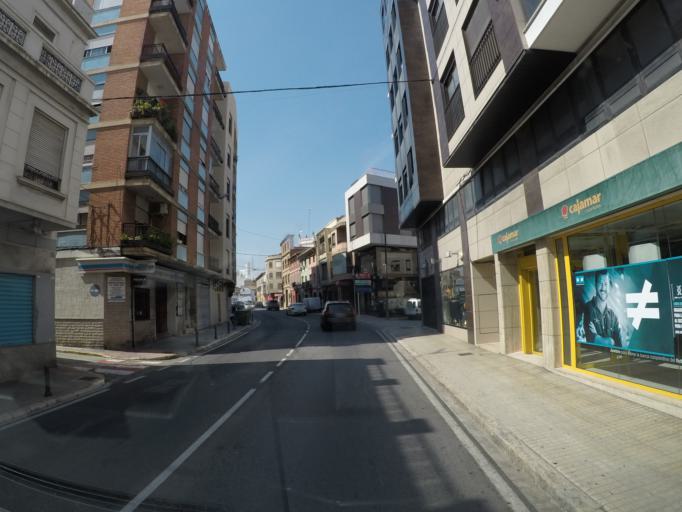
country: ES
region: Valencia
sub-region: Provincia de Valencia
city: Oliva
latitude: 38.9216
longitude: -0.1204
